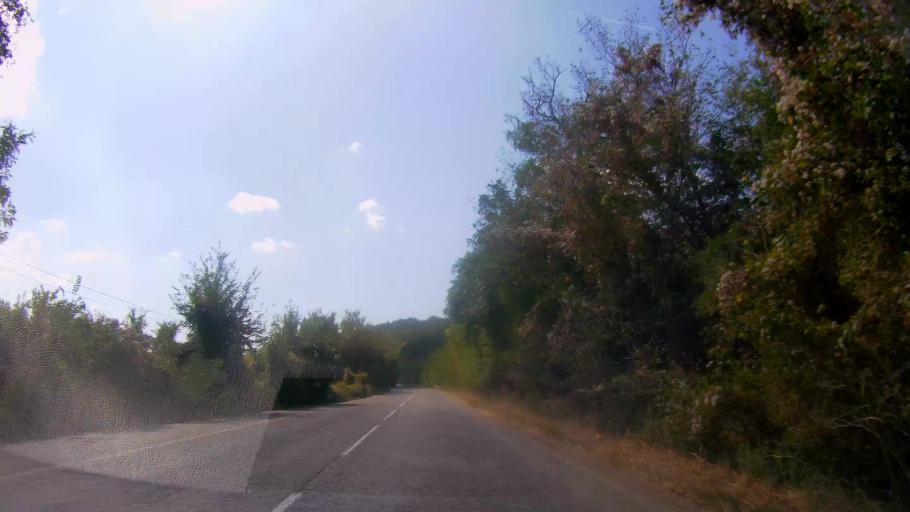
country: BG
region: Veliko Turnovo
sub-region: Obshtina Polski Trumbesh
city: Polski Trumbesh
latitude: 43.4407
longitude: 25.6547
